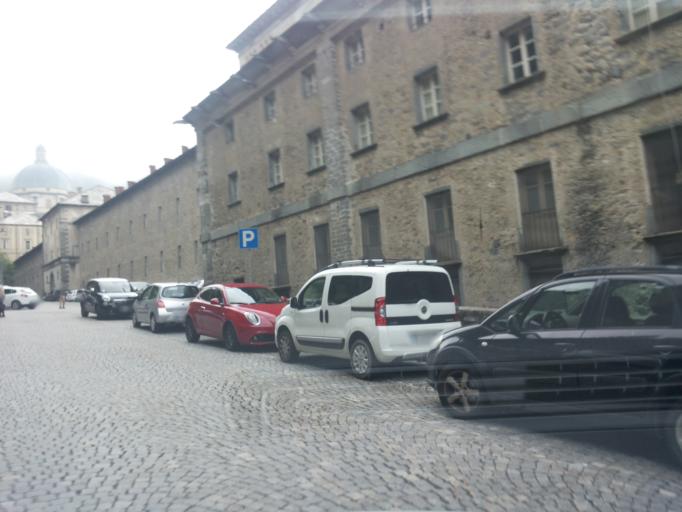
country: IT
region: Piedmont
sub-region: Provincia di Biella
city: San Paolo Cervo
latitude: 45.6261
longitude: 7.9810
